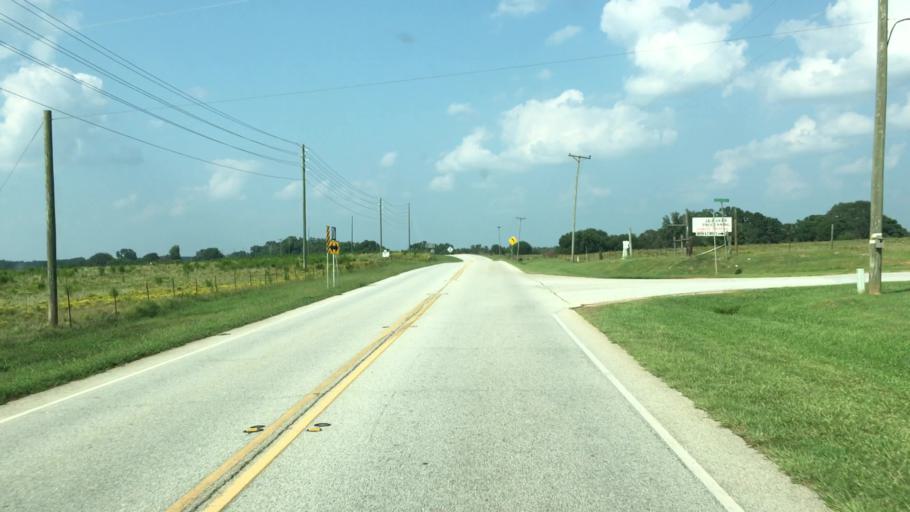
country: US
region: Georgia
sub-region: Newton County
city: Covington
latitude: 33.4801
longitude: -83.7461
